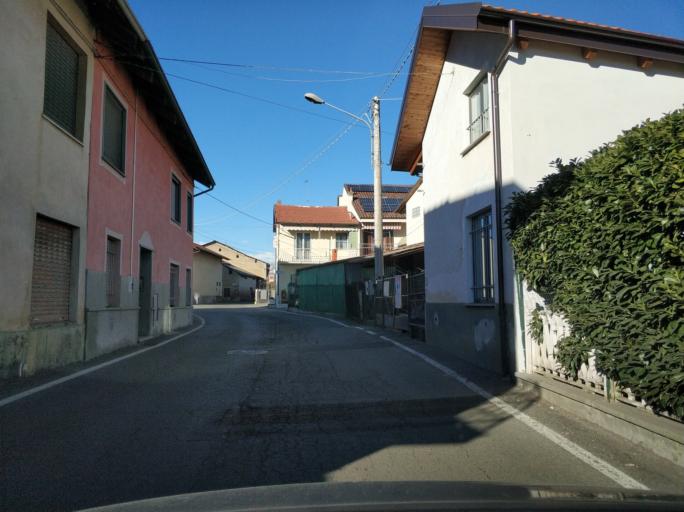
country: IT
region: Piedmont
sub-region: Provincia di Torino
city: San Francesco al Campo
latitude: 45.2308
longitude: 7.6482
